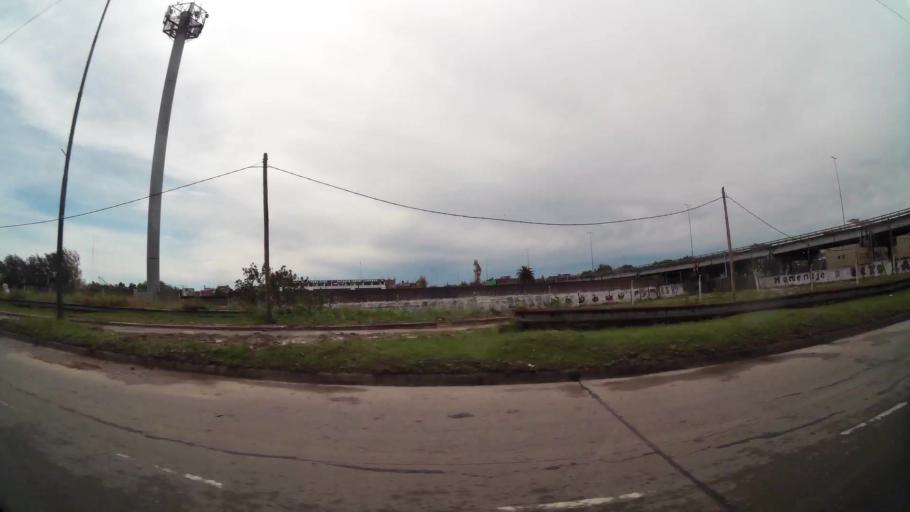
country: AR
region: Buenos Aires F.D.
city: Villa Lugano
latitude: -34.6654
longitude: -58.4512
